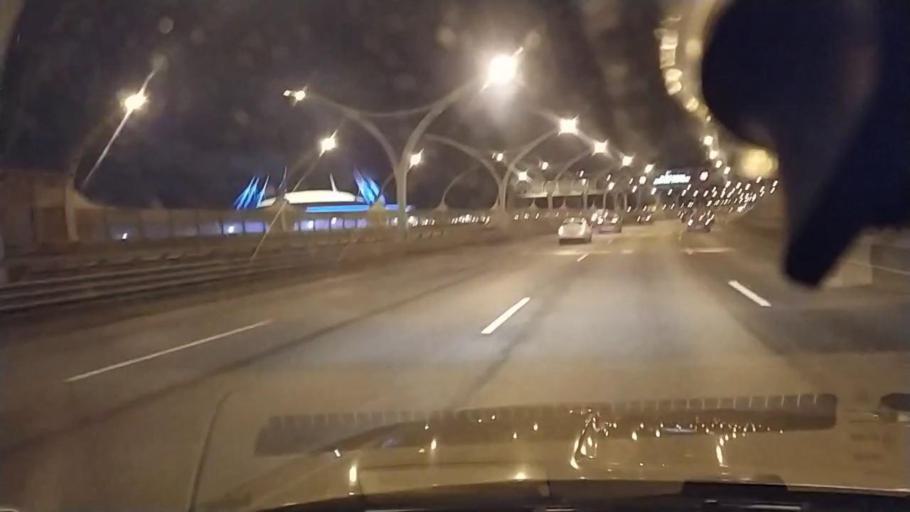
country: RU
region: St.-Petersburg
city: Staraya Derevnya
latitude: 59.9814
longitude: 30.2267
